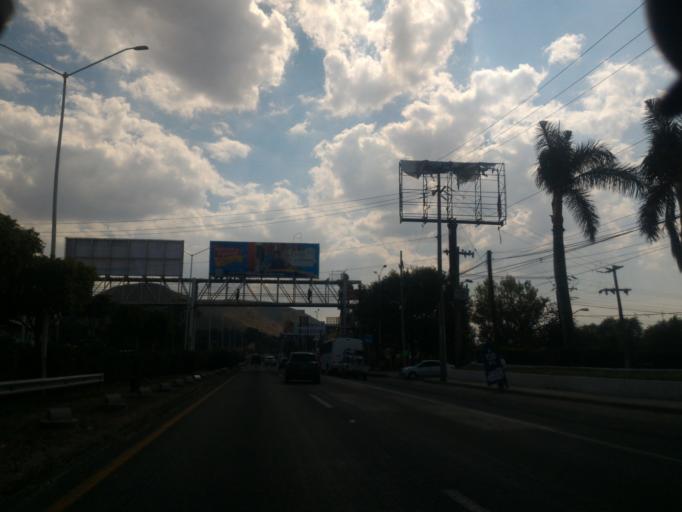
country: MX
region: Jalisco
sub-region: Tlajomulco de Zuniga
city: Lomas de San Agustin
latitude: 20.5364
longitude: -103.4746
